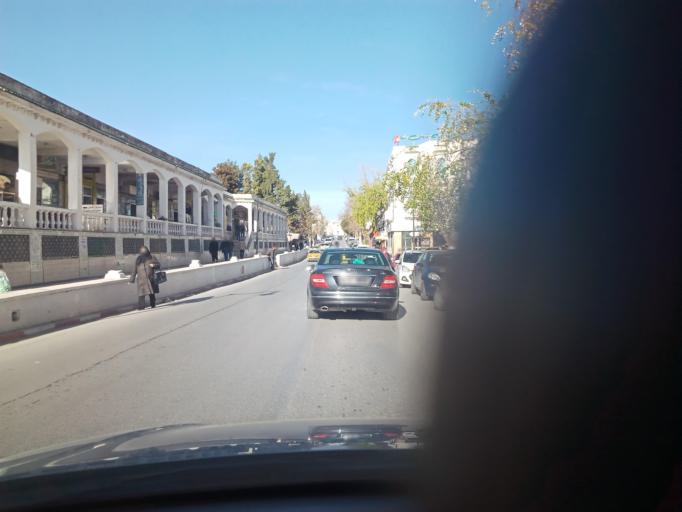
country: TN
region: Kef
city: El Kef
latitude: 36.1786
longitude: 8.7134
